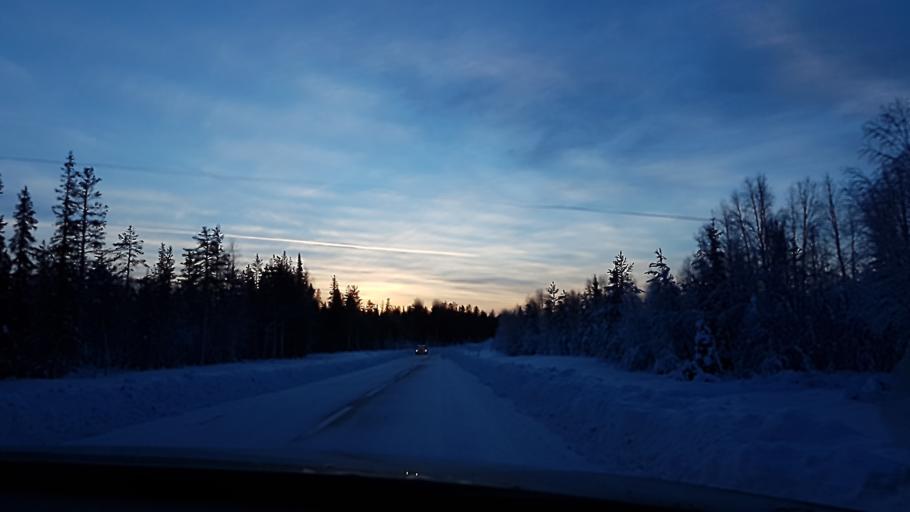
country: SE
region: Norrbotten
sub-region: Jokkmokks Kommun
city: Jokkmokk
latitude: 66.0834
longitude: 20.0731
